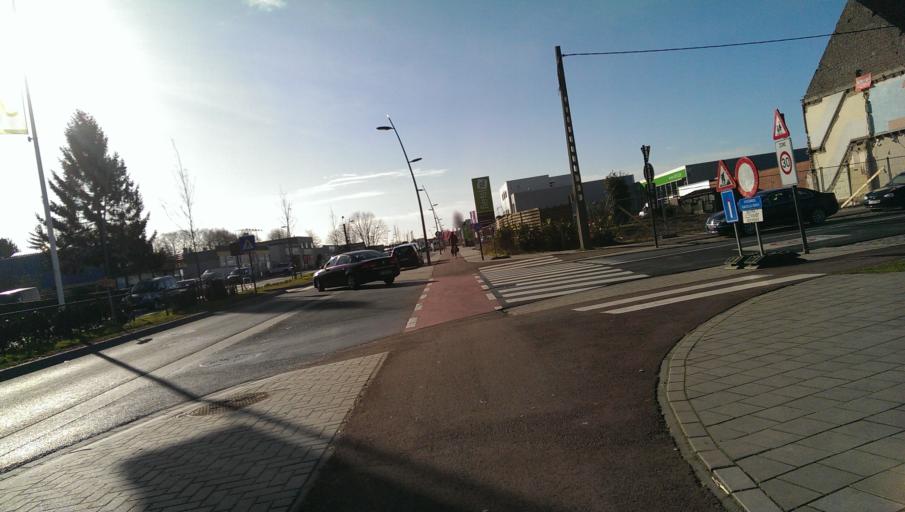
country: BE
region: Flanders
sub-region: Provincie West-Vlaanderen
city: Roeselare
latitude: 50.9446
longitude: 3.1133
